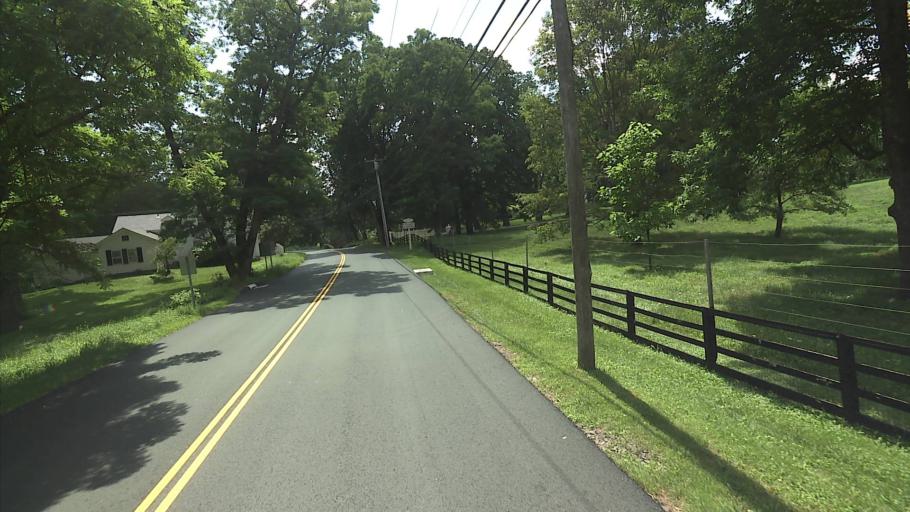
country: US
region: Connecticut
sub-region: Litchfield County
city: Canaan
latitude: 41.9577
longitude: -73.3652
